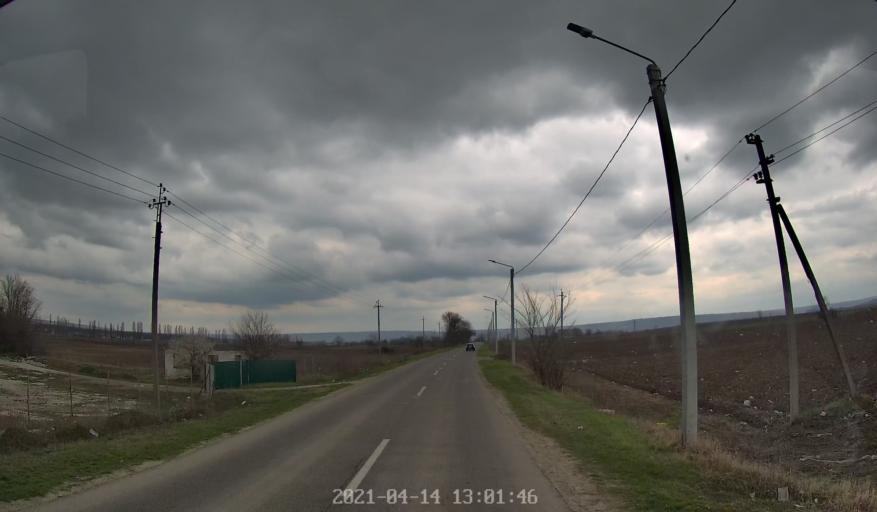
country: MD
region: Chisinau
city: Vadul lui Voda
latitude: 47.1290
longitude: 29.1144
